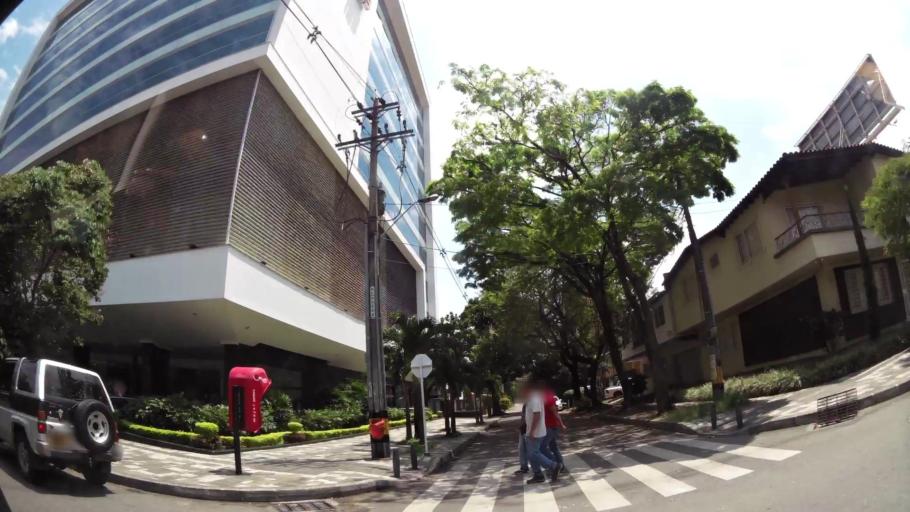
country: CO
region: Antioquia
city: Medellin
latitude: 6.2388
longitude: -75.6010
